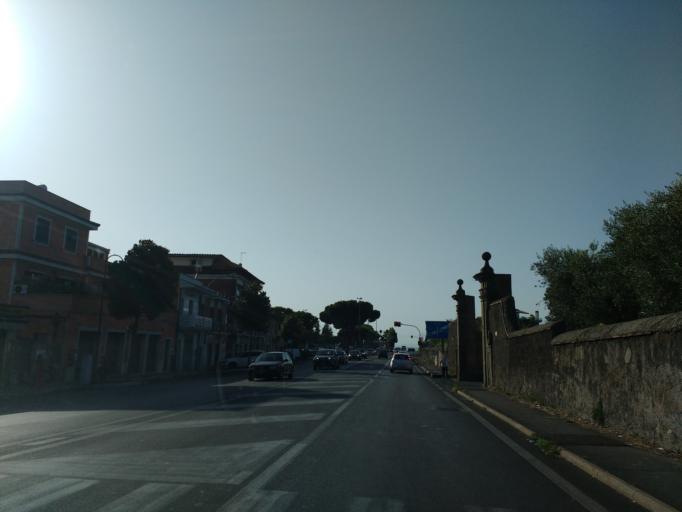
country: IT
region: Latium
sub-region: Citta metropolitana di Roma Capitale
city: Marino
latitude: 41.7655
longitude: 12.6179
